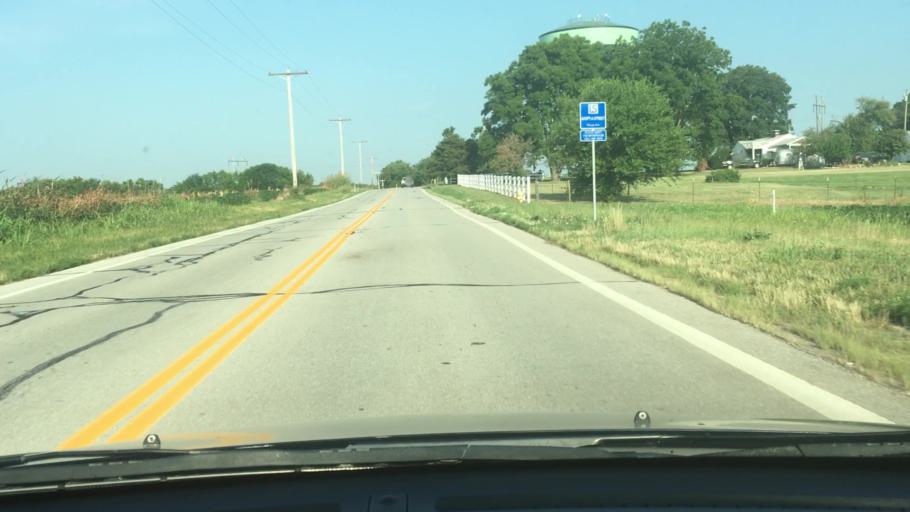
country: US
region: Missouri
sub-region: Jackson County
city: Lees Summit
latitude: 38.8902
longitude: -94.4163
